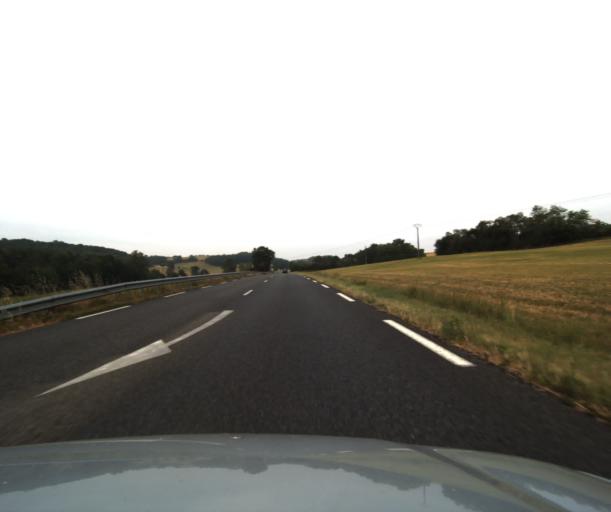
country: FR
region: Midi-Pyrenees
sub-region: Departement du Gers
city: Pavie
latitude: 43.5656
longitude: 0.5203
